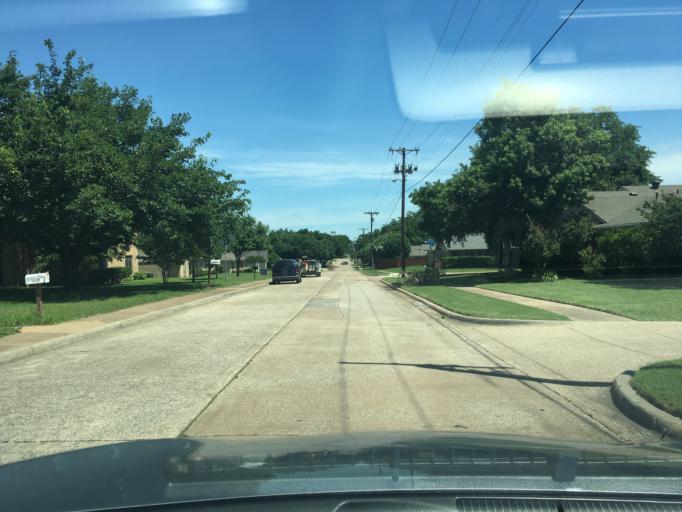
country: US
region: Texas
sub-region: Dallas County
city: Richardson
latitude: 32.9462
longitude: -96.6956
